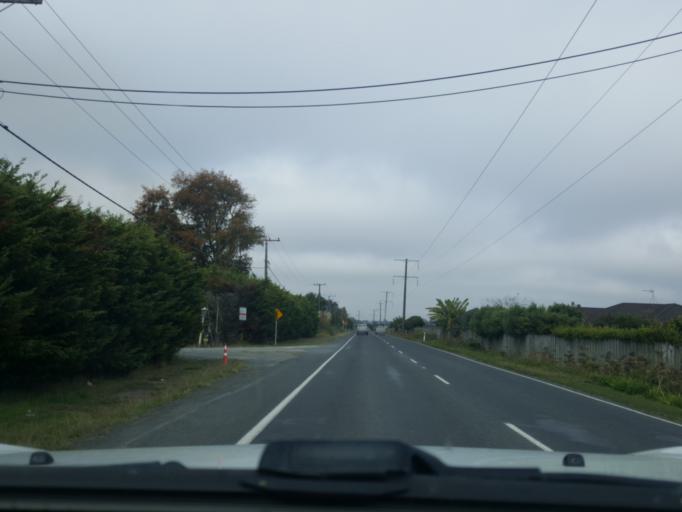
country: NZ
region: Waikato
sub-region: Hamilton City
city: Hamilton
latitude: -37.7362
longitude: 175.2883
